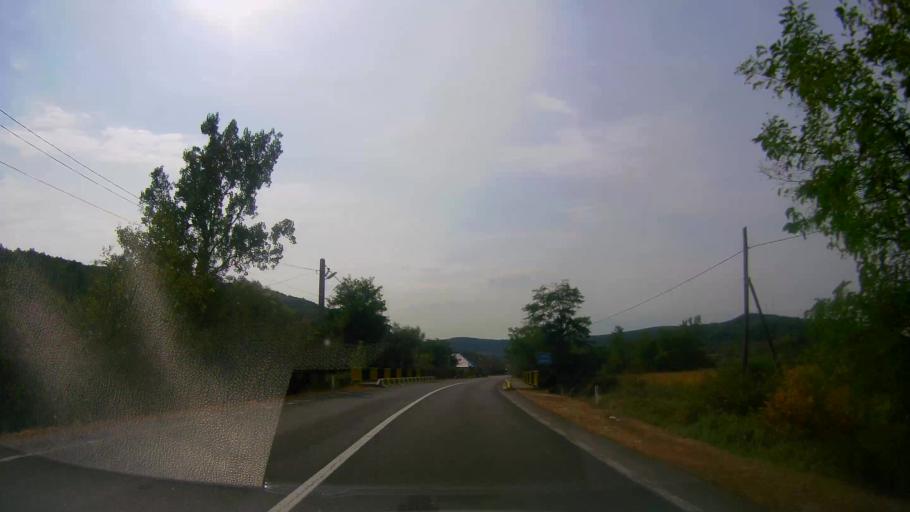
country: RO
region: Salaj
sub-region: Comuna Zimbor
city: Zimbor
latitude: 46.9902
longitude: 23.2515
